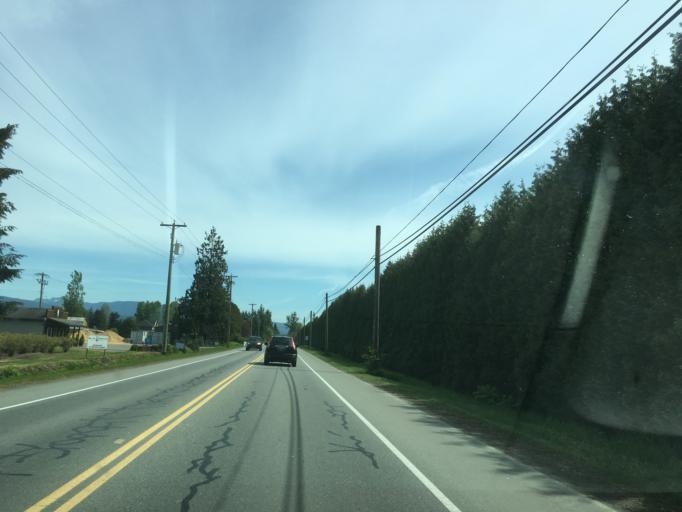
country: CA
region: British Columbia
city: Pitt Meadows
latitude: 49.2443
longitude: -122.7084
